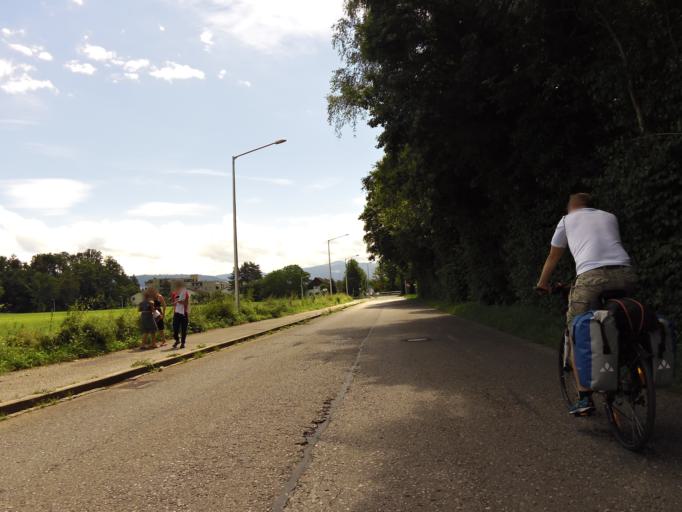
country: AT
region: Vorarlberg
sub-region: Politischer Bezirk Bregenz
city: Hard
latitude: 47.5014
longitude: 9.7038
